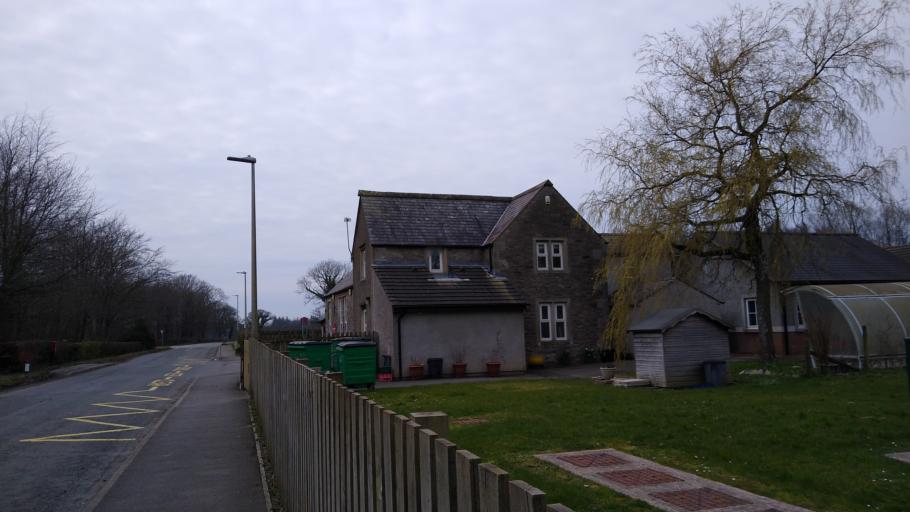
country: GB
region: England
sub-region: Cumbria
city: Cockermouth
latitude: 54.6879
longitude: -3.3887
